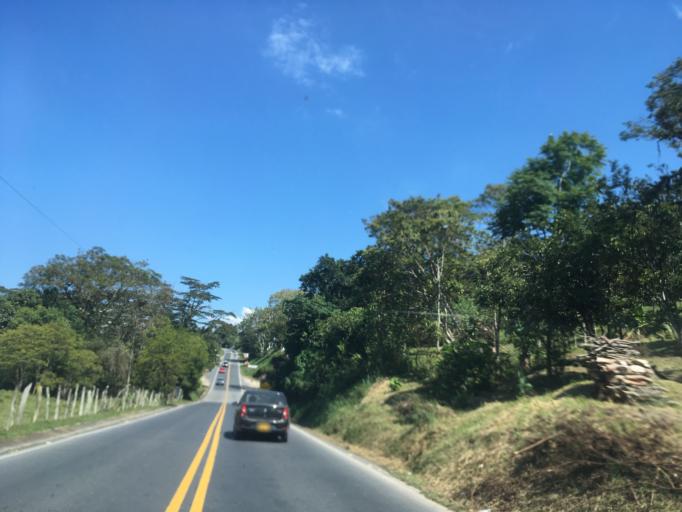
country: CO
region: Santander
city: Suaita
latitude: 6.0794
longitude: -73.3955
